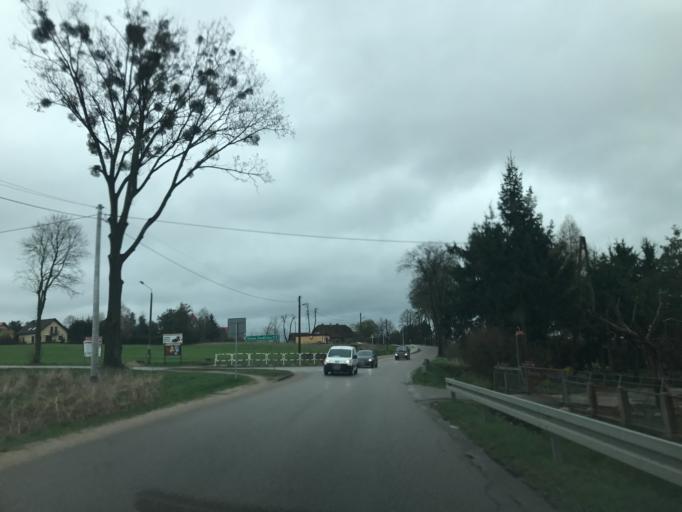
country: PL
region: Warmian-Masurian Voivodeship
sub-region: Powiat ostrodzki
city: Ostroda
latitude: 53.7017
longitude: 20.0217
